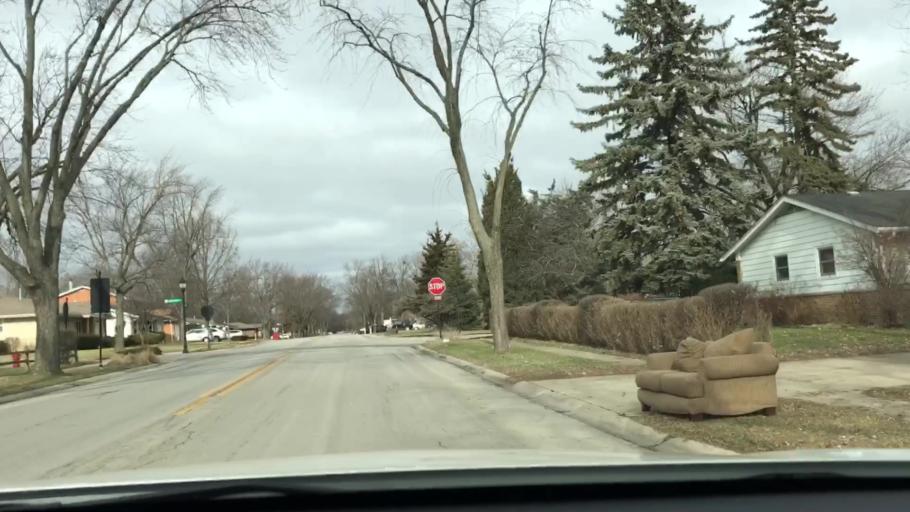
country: US
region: Illinois
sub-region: Cook County
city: Elk Grove Village
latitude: 42.0106
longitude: -87.9892
